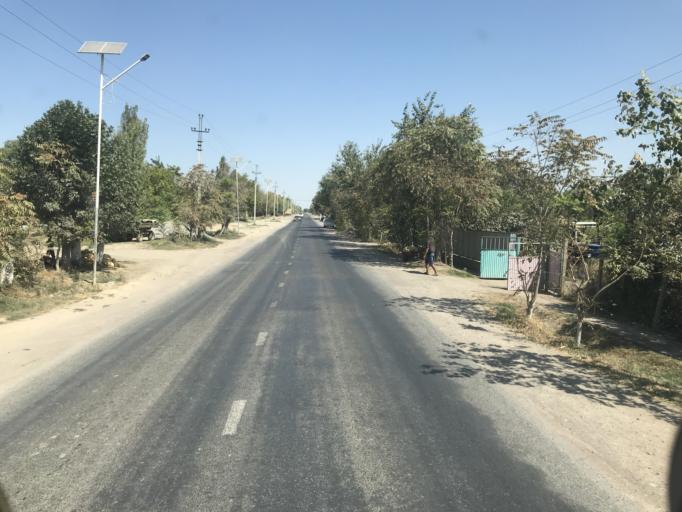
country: KZ
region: Ongtustik Qazaqstan
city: Ilyich
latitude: 40.9360
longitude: 68.4883
